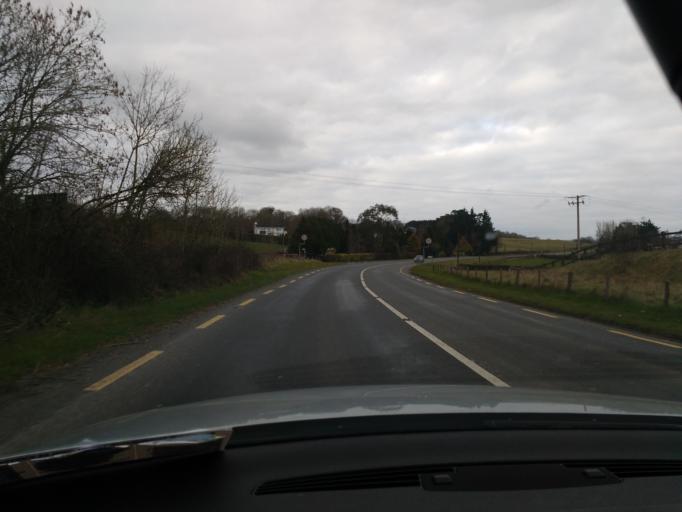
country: IE
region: Leinster
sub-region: Kilkenny
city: Kilkenny
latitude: 52.6769
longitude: -7.2746
